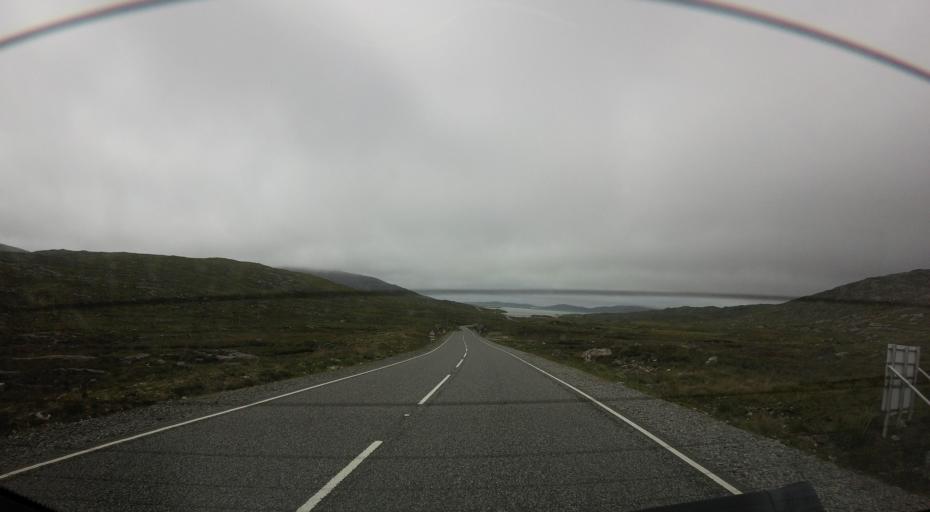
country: GB
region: Scotland
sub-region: Eilean Siar
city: Harris
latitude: 57.8665
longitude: -6.8840
